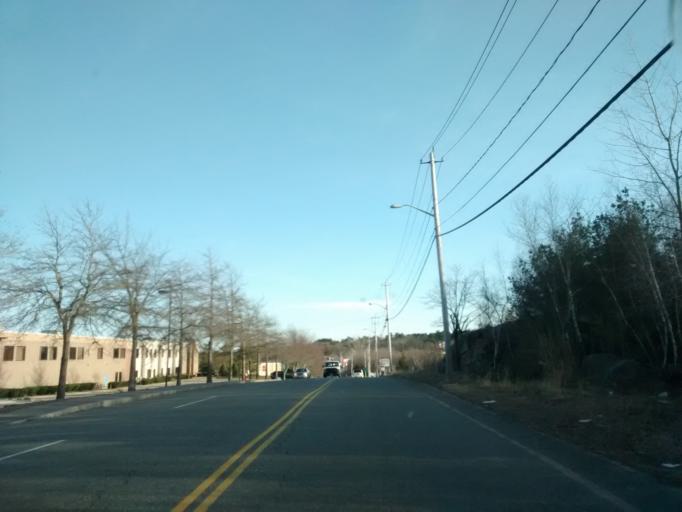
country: US
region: Massachusetts
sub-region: Norfolk County
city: Avon
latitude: 42.1334
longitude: -71.0675
